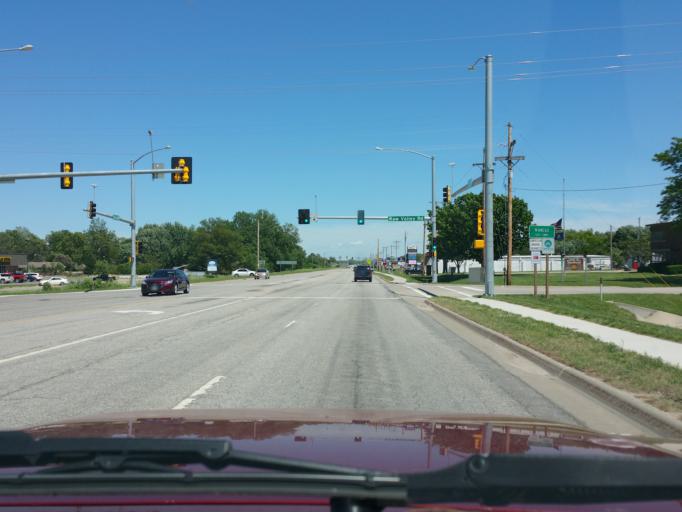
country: US
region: Kansas
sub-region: Pottawatomie County
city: Wamego
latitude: 39.2101
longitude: -96.3157
